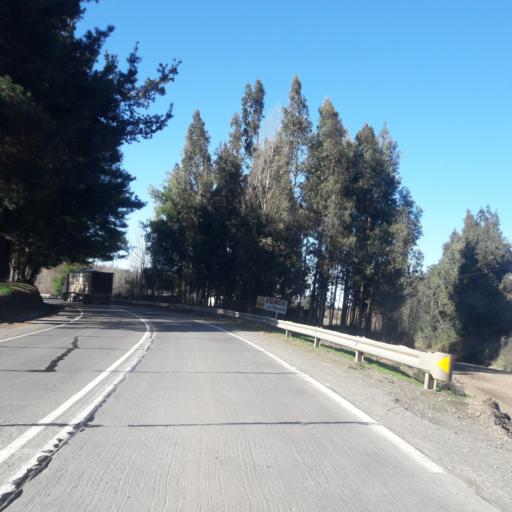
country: CL
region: Araucania
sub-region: Provincia de Malleco
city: Angol
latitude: -37.7413
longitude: -72.6119
